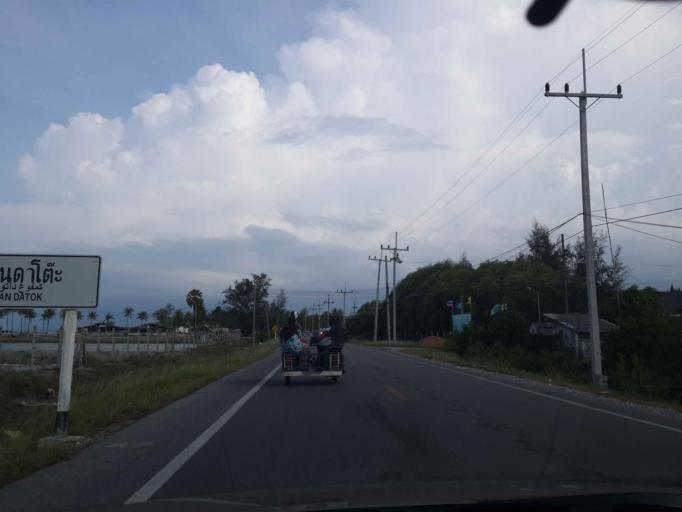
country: TH
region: Pattani
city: Yaring
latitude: 6.9204
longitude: 101.3319
